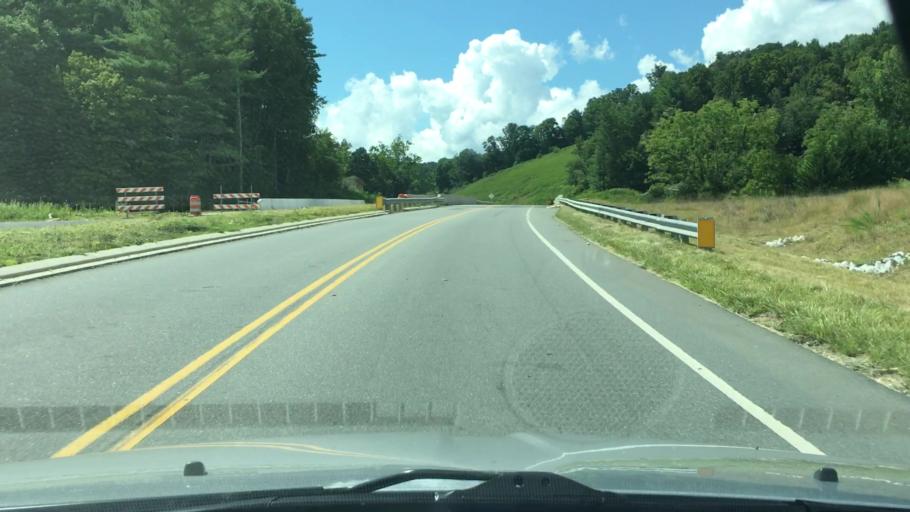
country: US
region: North Carolina
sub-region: Yancey County
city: Burnsville
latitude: 35.9090
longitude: -82.2187
